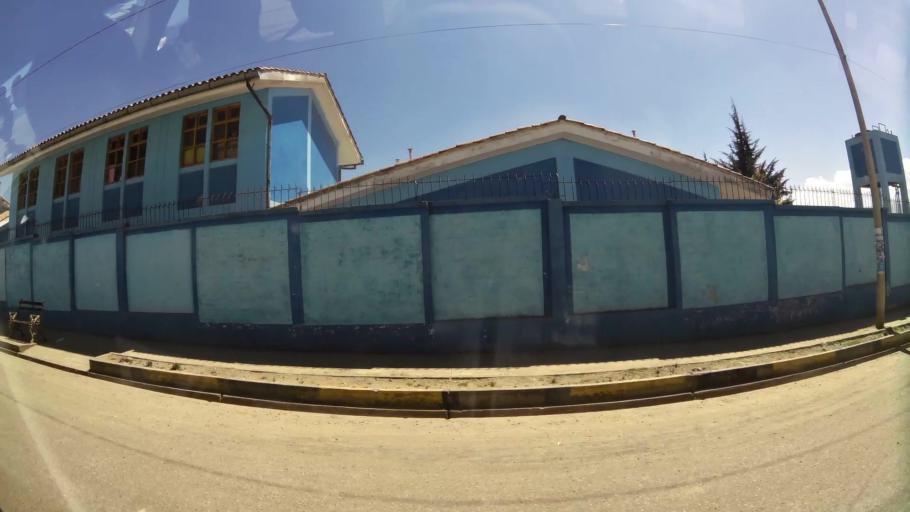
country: PE
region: Junin
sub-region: Provincia de Jauja
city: Jauja
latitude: -11.7692
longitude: -75.5010
